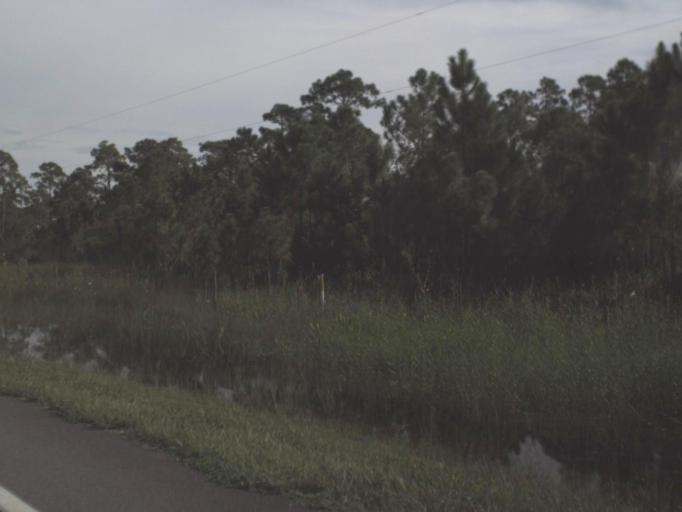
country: US
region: Florida
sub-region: Lee County
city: Olga
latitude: 26.8395
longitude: -81.7598
